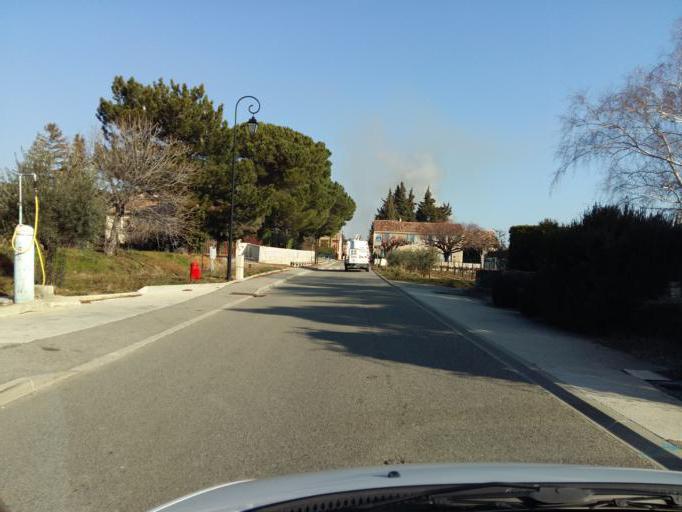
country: FR
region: Provence-Alpes-Cote d'Azur
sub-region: Departement du Vaucluse
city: Vaison-la-Romaine
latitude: 44.2501
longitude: 5.0188
